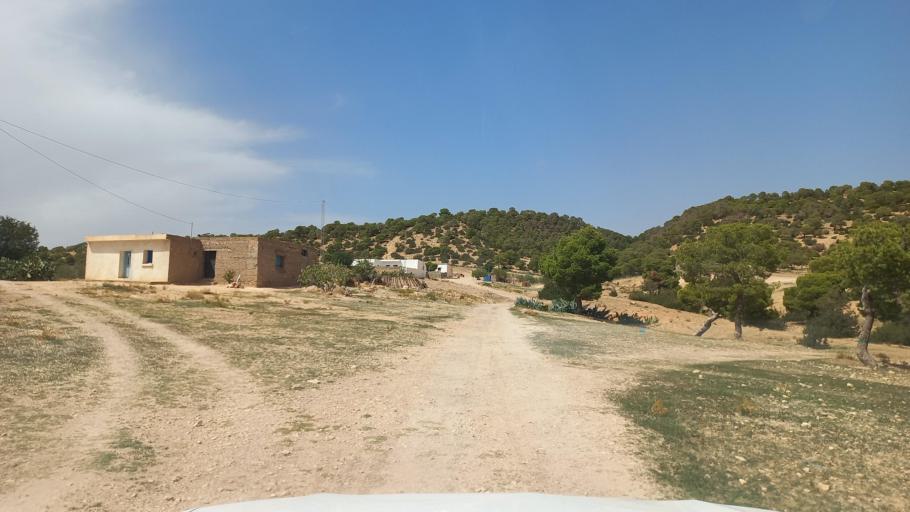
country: TN
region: Al Qasrayn
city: Kasserine
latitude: 35.3736
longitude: 8.8961
